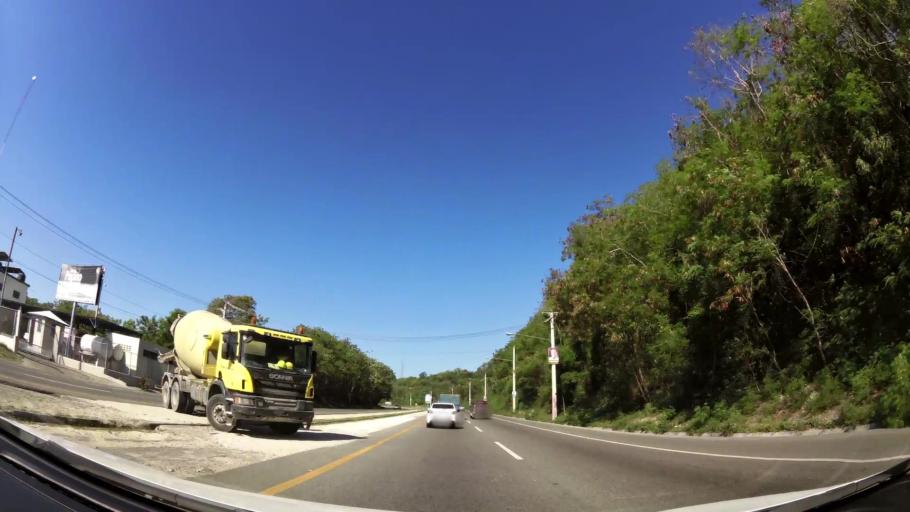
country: DO
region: San Cristobal
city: El Carril
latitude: 18.4376
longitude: -70.0211
